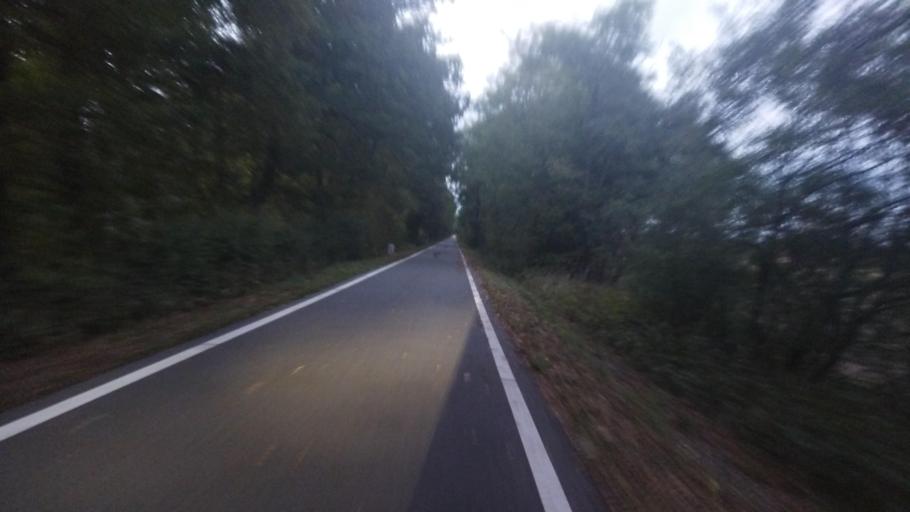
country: DE
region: North Rhine-Westphalia
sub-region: Regierungsbezirk Munster
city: Horstmar
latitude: 52.1070
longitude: 7.3347
